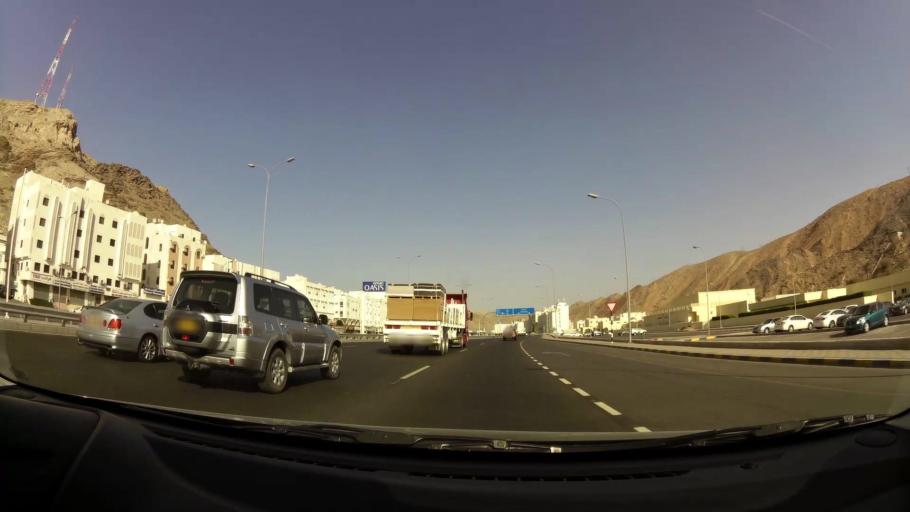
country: OM
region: Muhafazat Masqat
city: Muscat
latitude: 23.5901
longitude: 58.5314
